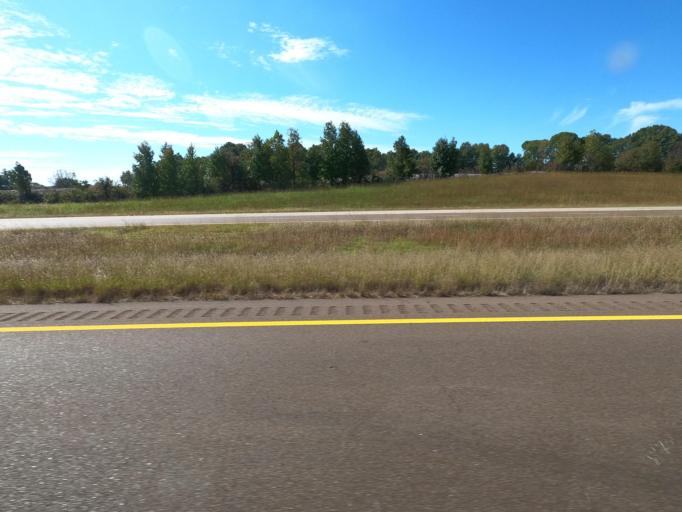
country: US
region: Tennessee
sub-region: Dyer County
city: Dyersburg
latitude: 35.9622
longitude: -89.3275
